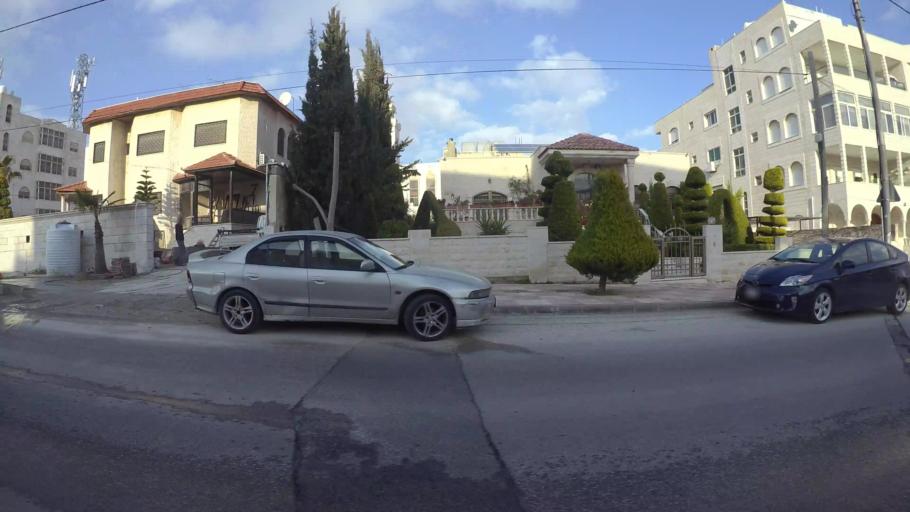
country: JO
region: Amman
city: Wadi as Sir
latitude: 31.9821
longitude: 35.8510
